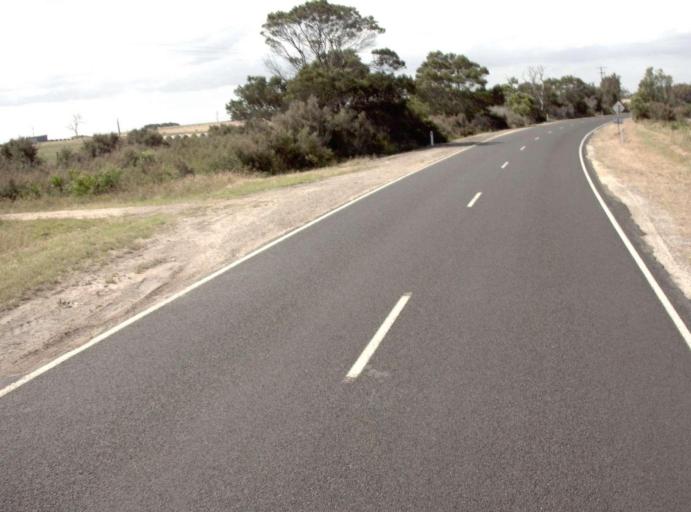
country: AU
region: Victoria
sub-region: Wellington
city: Sale
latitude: -38.3542
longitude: 147.1712
